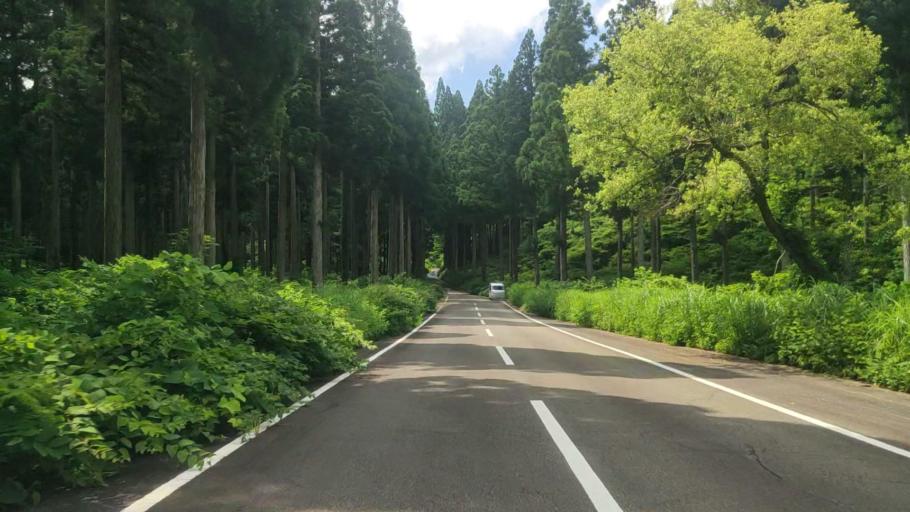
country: JP
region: Fukui
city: Katsuyama
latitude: 36.1849
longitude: 136.5233
